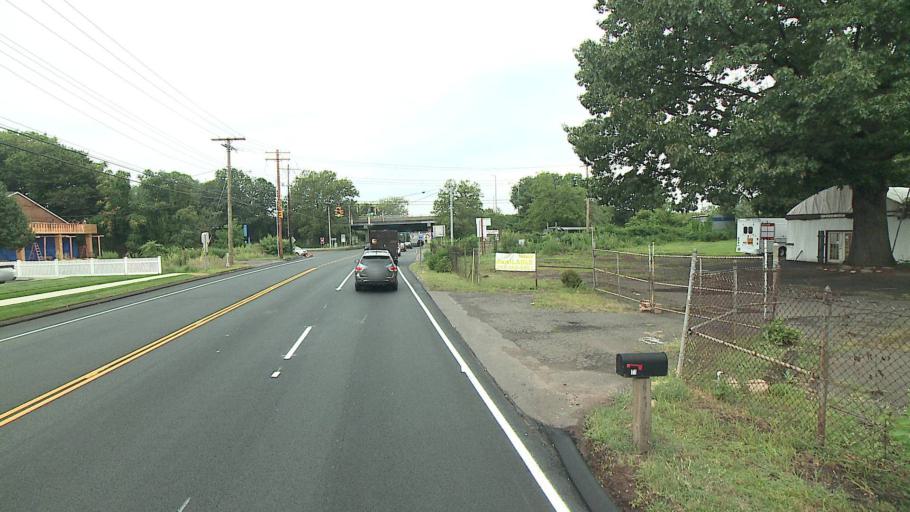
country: US
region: Connecticut
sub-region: New Haven County
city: North Haven
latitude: 41.3508
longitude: -72.8657
